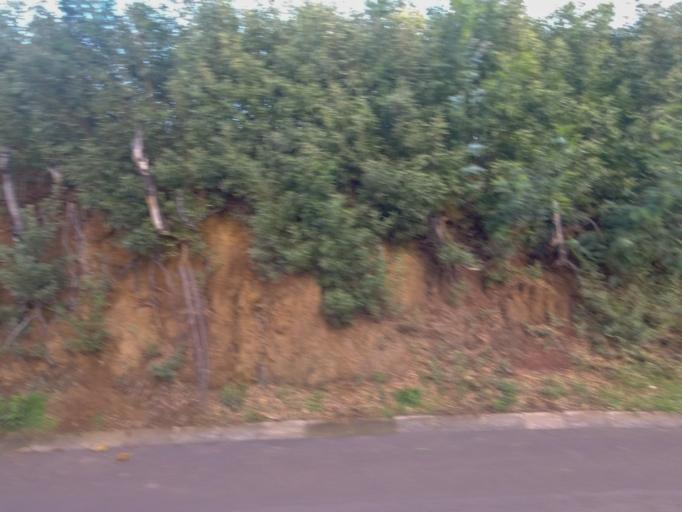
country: PT
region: Madeira
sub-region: Funchal
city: Nossa Senhora do Monte
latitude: 32.6709
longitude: -16.8903
